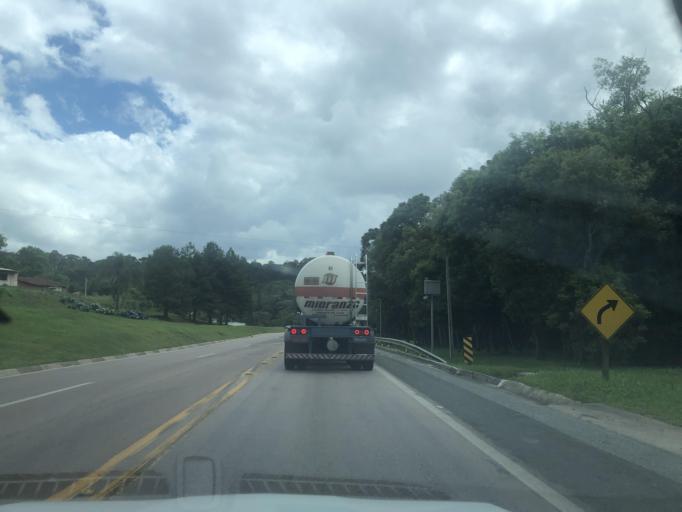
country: BR
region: Parana
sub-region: Rio Negro
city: Rio Negro
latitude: -26.0742
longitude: -49.7447
